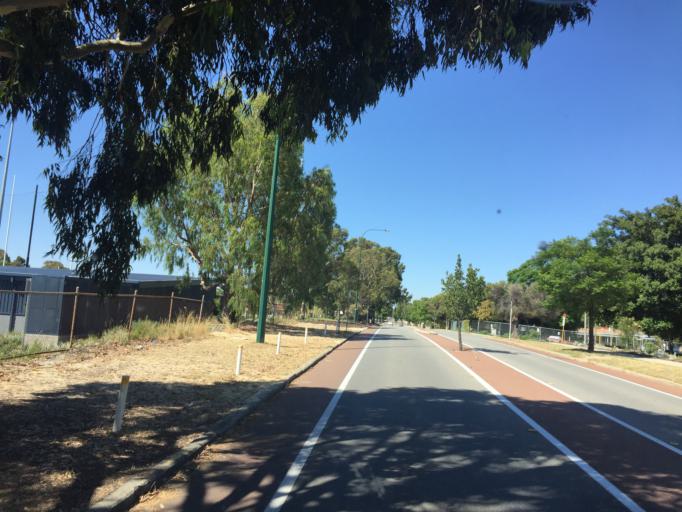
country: AU
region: Western Australia
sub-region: Victoria Park
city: Victoria Park
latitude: -31.9741
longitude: 115.9090
